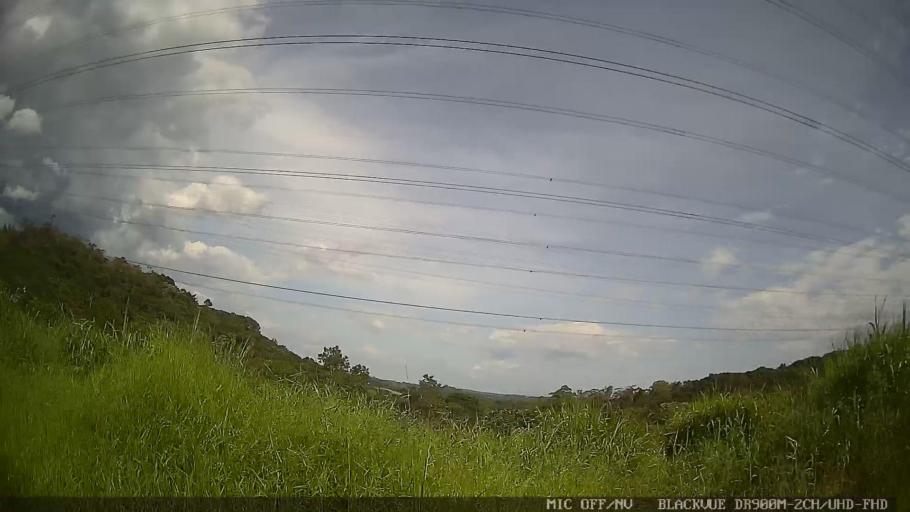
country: BR
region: Sao Paulo
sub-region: Mogi das Cruzes
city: Mogi das Cruzes
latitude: -23.6398
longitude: -46.2143
